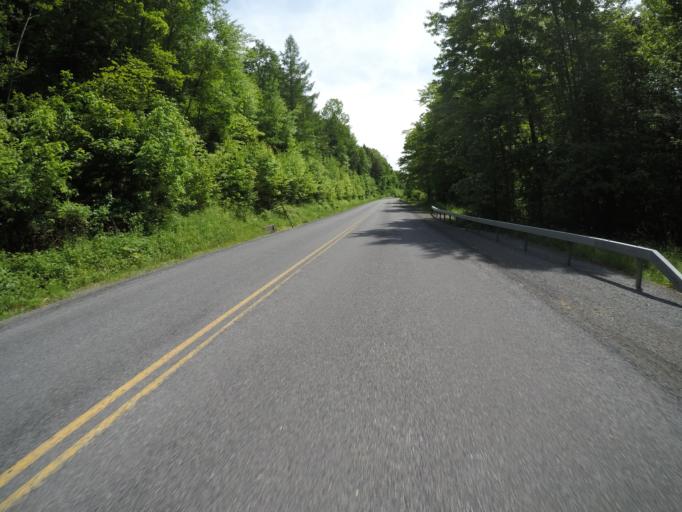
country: US
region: New York
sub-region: Delaware County
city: Delhi
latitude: 42.1081
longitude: -74.8227
